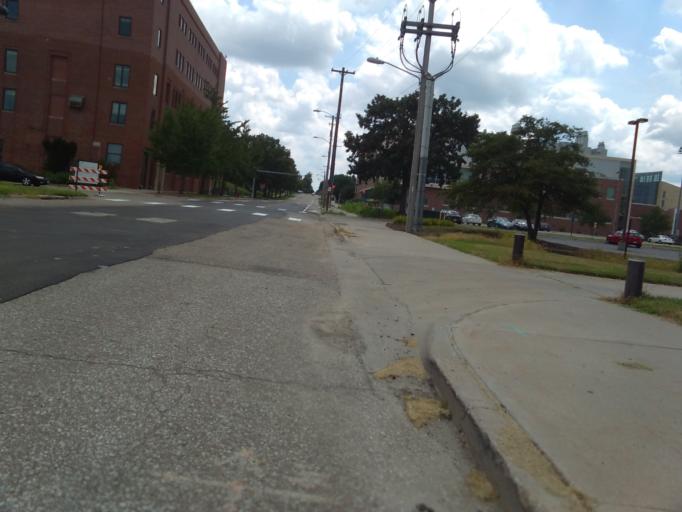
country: US
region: Nebraska
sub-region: Lancaster County
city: Lincoln
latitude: 40.8238
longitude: -96.6982
